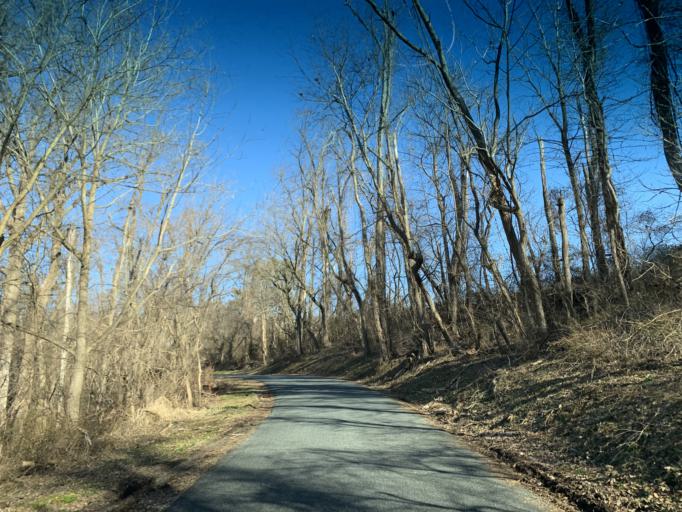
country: US
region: Maryland
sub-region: Harford County
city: South Bel Air
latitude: 39.6208
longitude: -76.2488
